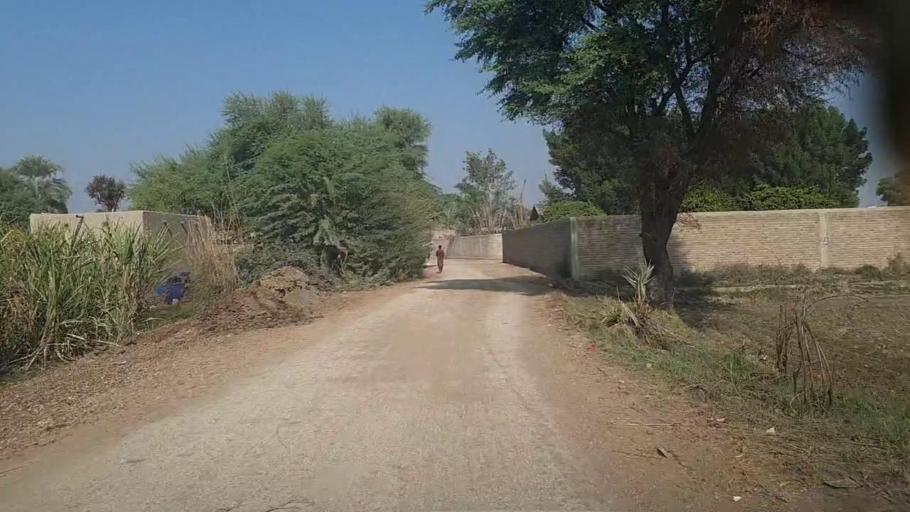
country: PK
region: Sindh
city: Karaundi
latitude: 26.9765
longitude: 68.4502
